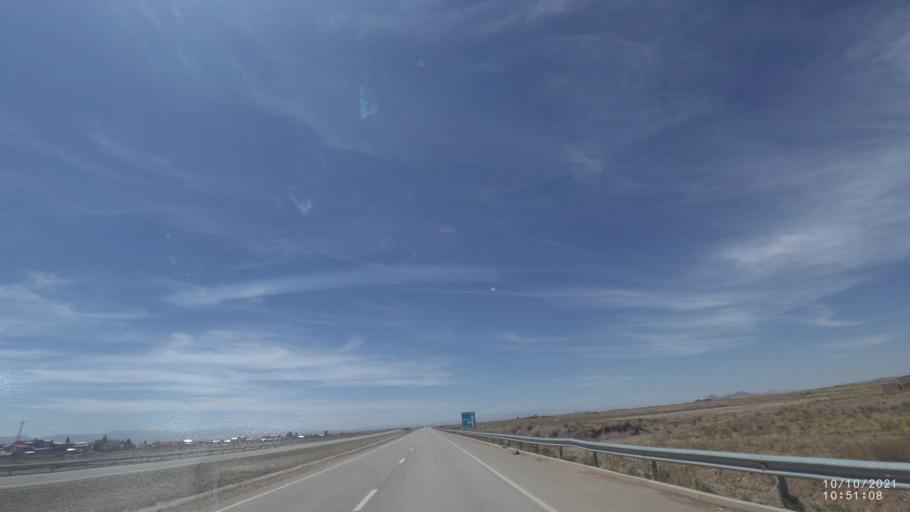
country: BO
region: La Paz
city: Colquiri
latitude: -17.6505
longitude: -67.2157
